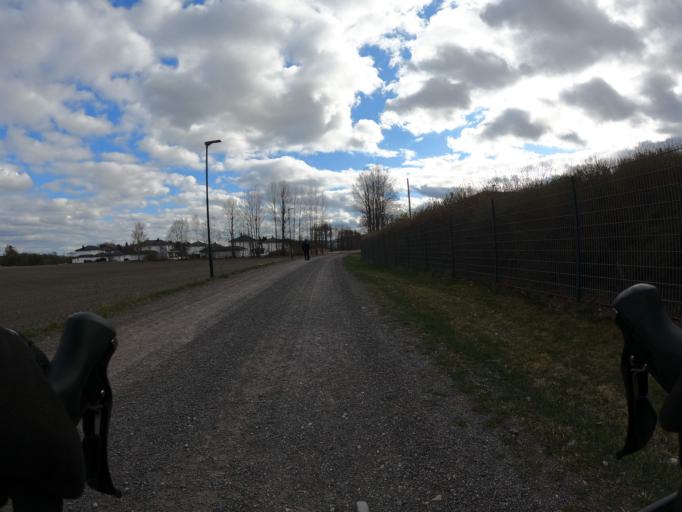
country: NO
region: Akershus
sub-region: Skedsmo
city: Leirsund
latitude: 59.9713
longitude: 11.0745
